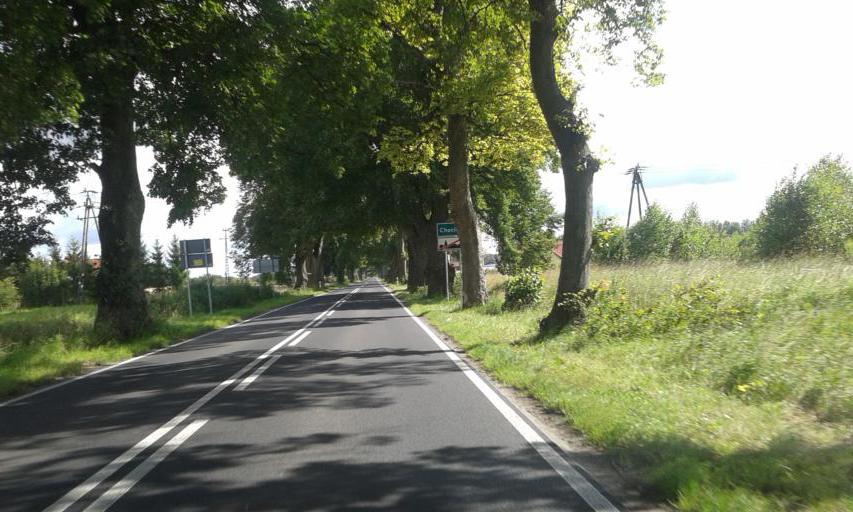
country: PL
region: West Pomeranian Voivodeship
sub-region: Powiat koszalinski
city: Bobolice
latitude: 53.9606
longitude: 16.5999
